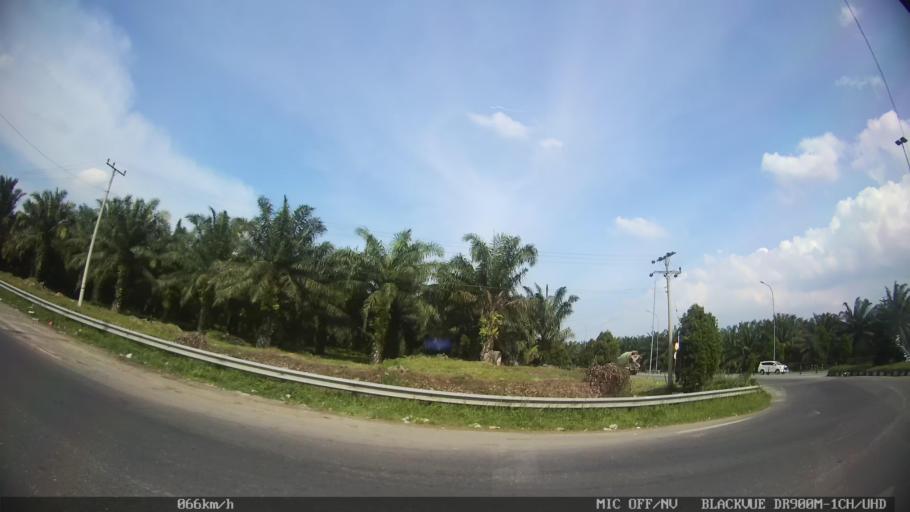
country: ID
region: North Sumatra
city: Binjai
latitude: 3.6475
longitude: 98.5355
